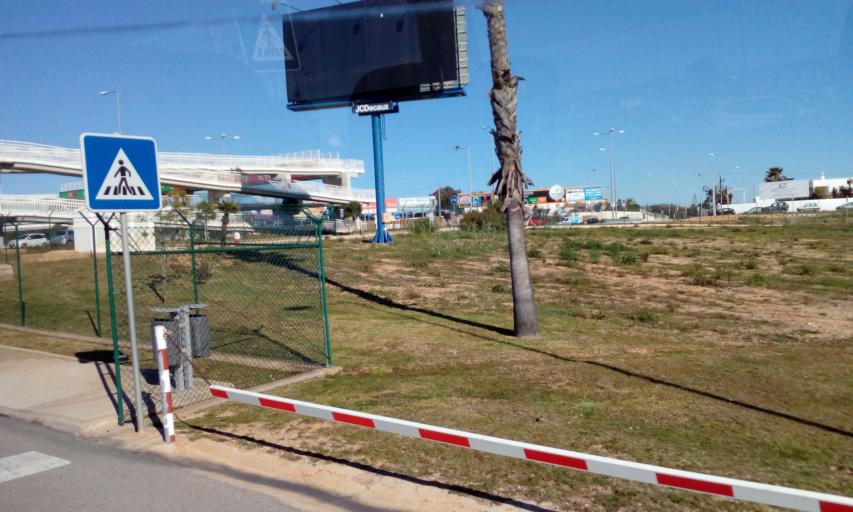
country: PT
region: Faro
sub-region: Faro
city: Faro
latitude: 37.0226
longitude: -7.9698
